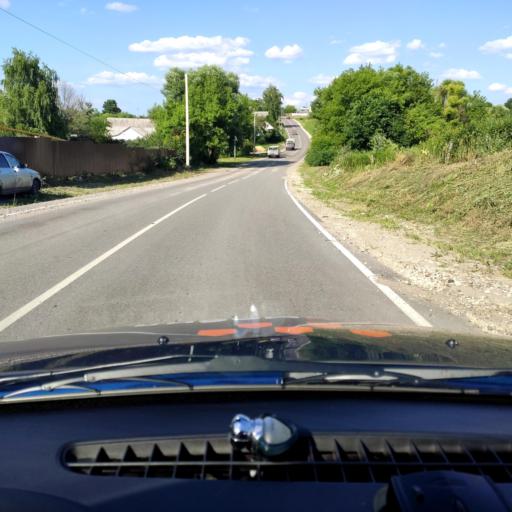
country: RU
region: Voronezj
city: Devitsa
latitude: 51.6450
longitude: 38.9627
